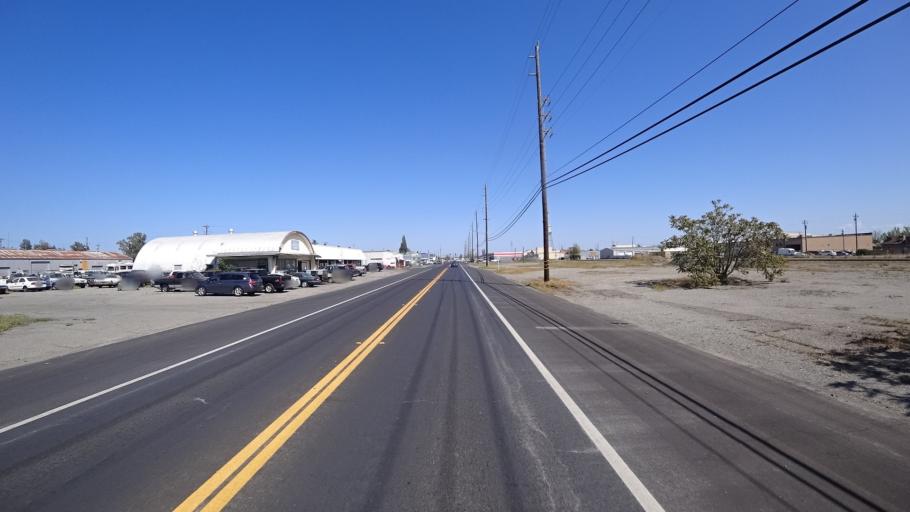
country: US
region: California
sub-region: Glenn County
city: Orland
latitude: 39.7443
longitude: -122.1976
